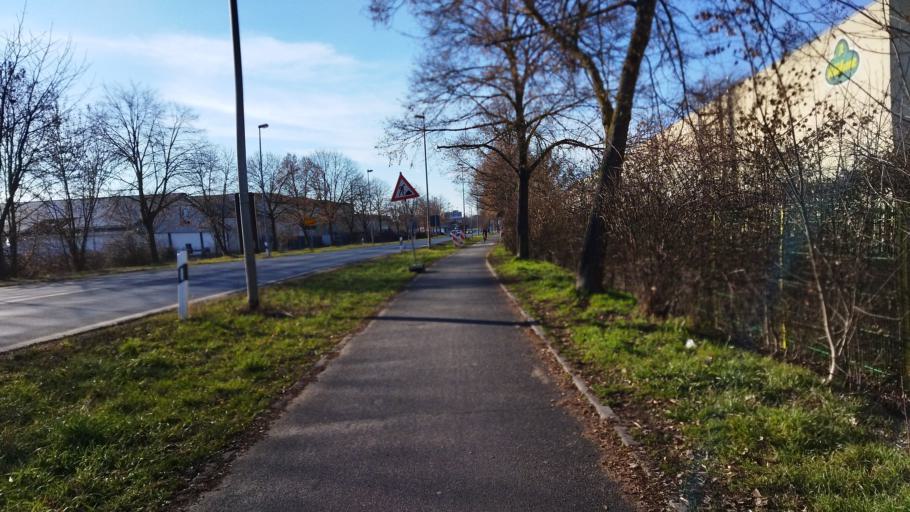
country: DE
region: Bavaria
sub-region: Regierungsbezirk Unterfranken
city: Sennfeld
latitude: 50.0375
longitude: 10.2505
